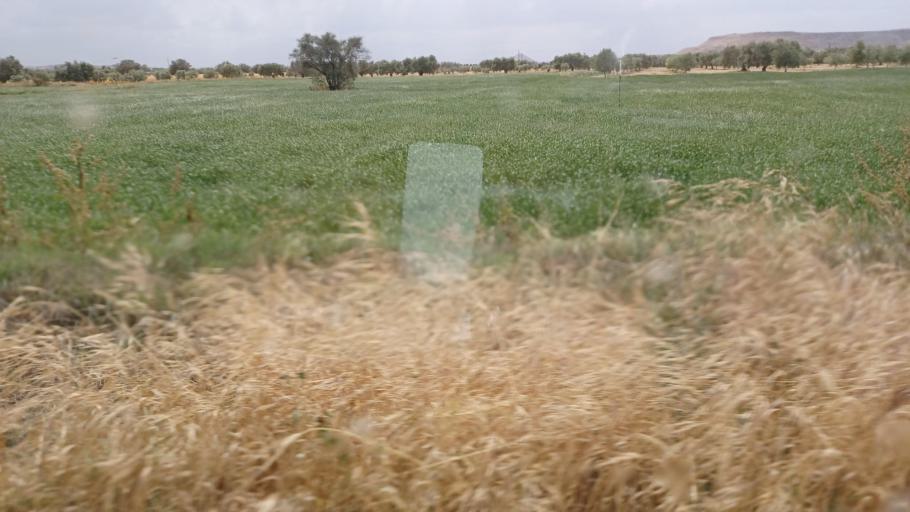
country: CY
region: Larnaka
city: Athienou
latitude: 35.0752
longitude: 33.5387
